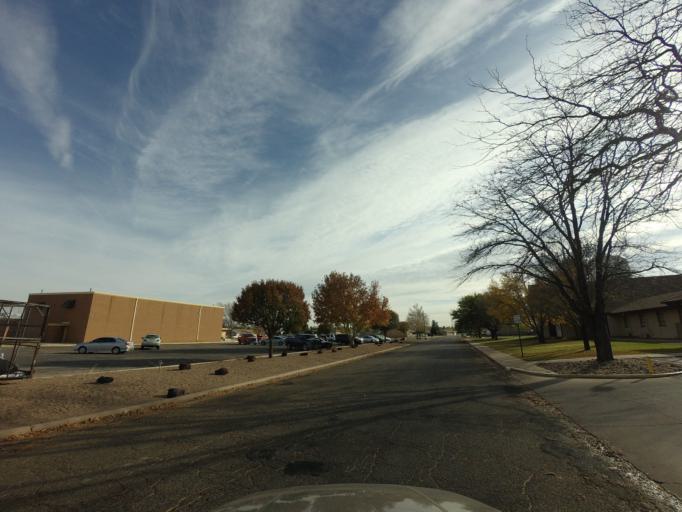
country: US
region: New Mexico
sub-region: Curry County
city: Clovis
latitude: 34.4277
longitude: -103.2264
